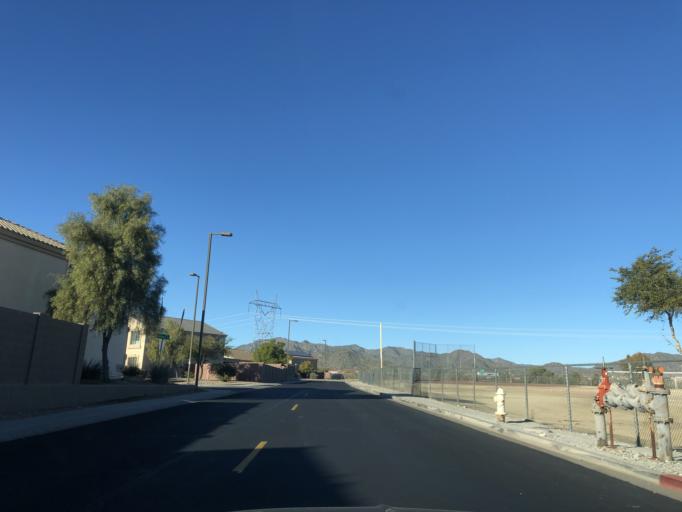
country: US
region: Arizona
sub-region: Maricopa County
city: Buckeye
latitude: 33.4389
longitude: -112.5639
